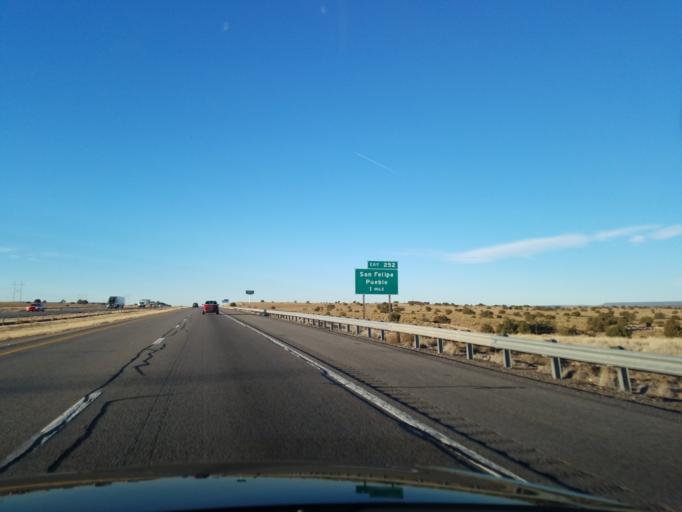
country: US
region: New Mexico
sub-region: Sandoval County
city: San Felipe Pueblo
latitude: 35.4301
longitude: -106.3851
